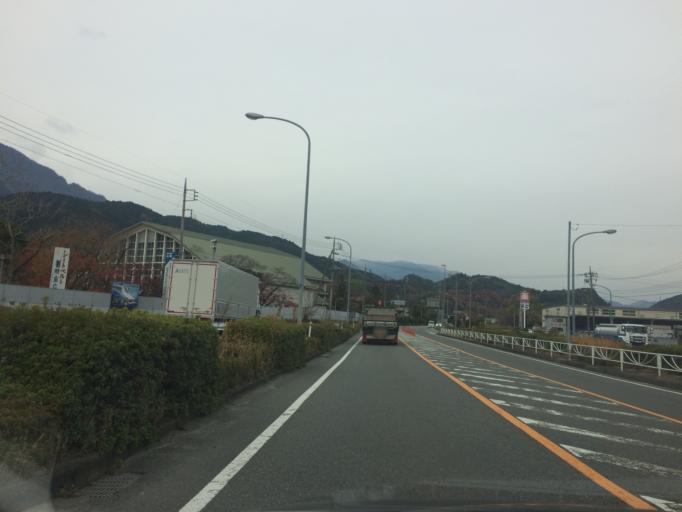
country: JP
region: Shizuoka
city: Fujinomiya
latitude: 35.2422
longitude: 138.4850
